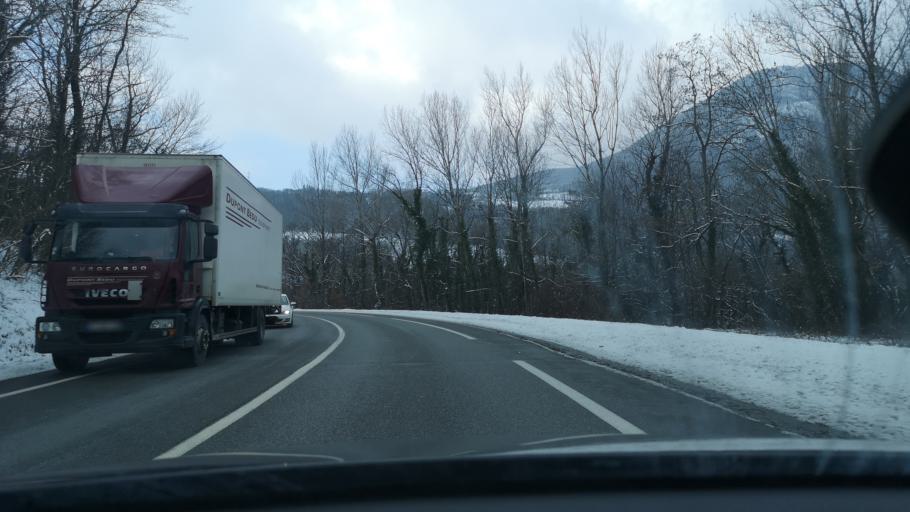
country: FR
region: Rhone-Alpes
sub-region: Departement de l'Ain
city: Collonges
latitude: 46.1017
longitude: 5.8789
